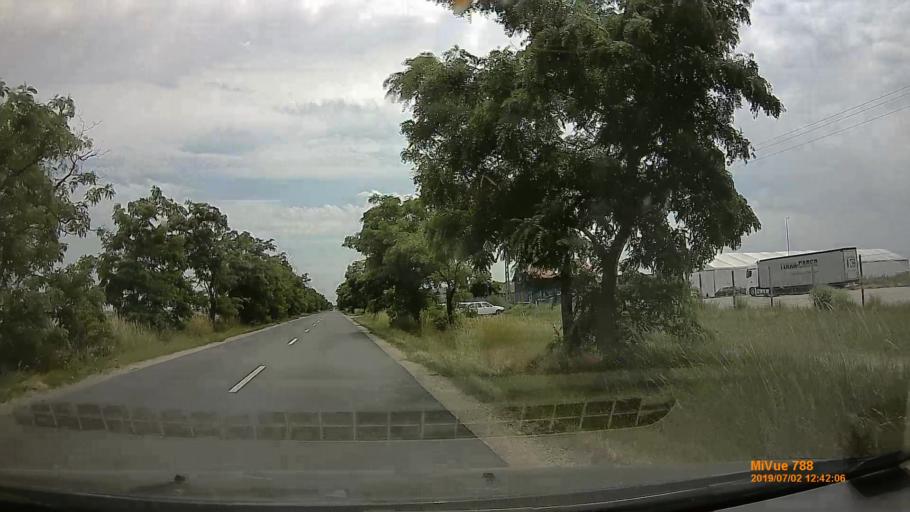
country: HU
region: Gyor-Moson-Sopron
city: Janossomorja
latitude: 47.8459
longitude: 17.1847
